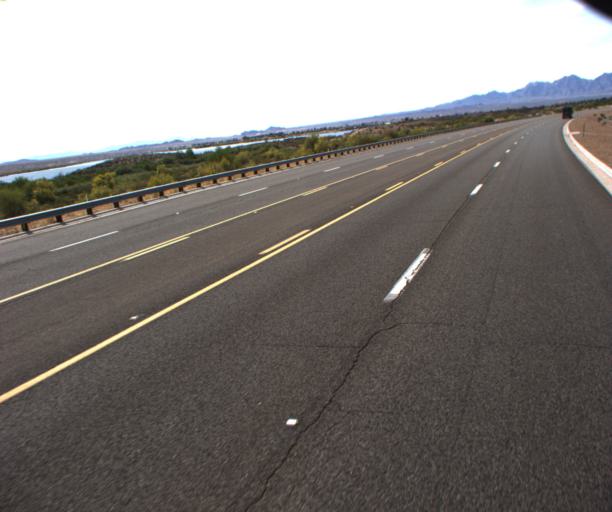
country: US
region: Arizona
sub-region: Mohave County
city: Lake Havasu City
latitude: 34.4538
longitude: -114.3244
